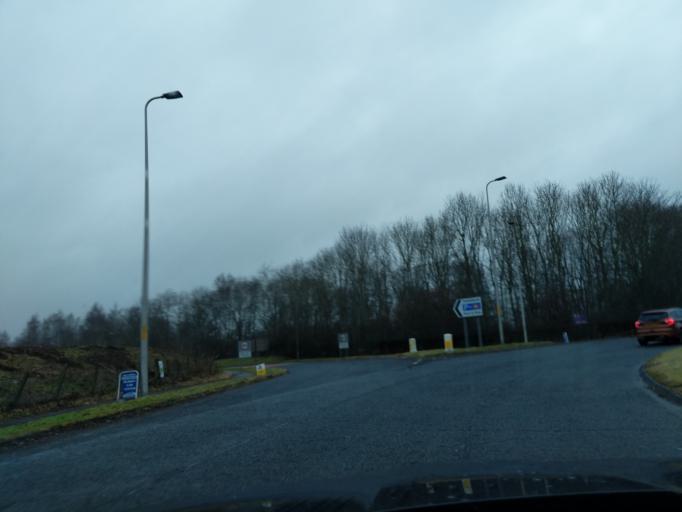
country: GB
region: Scotland
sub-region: The Scottish Borders
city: Melrose
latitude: 55.6018
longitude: -2.7518
